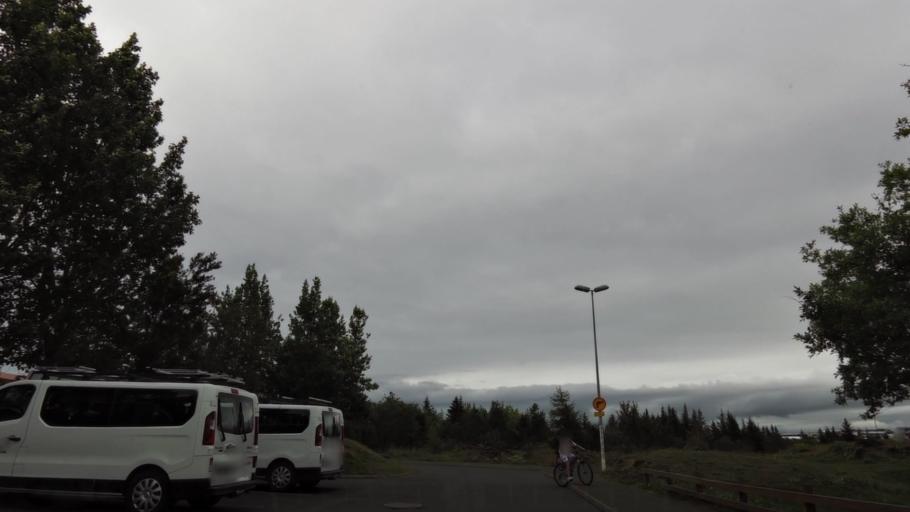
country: IS
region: Capital Region
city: Hafnarfjoerdur
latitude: 64.0822
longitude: -21.9575
